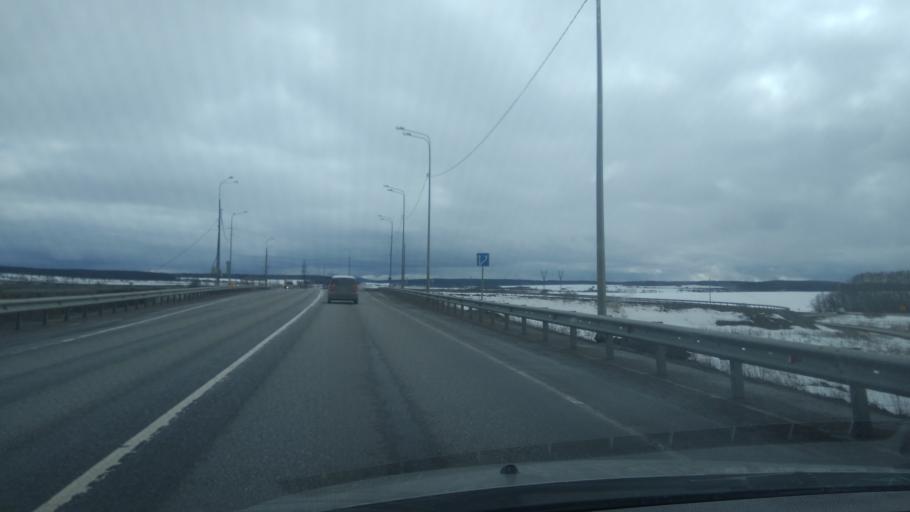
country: RU
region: Sverdlovsk
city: Achit
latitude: 56.7910
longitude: 57.8790
